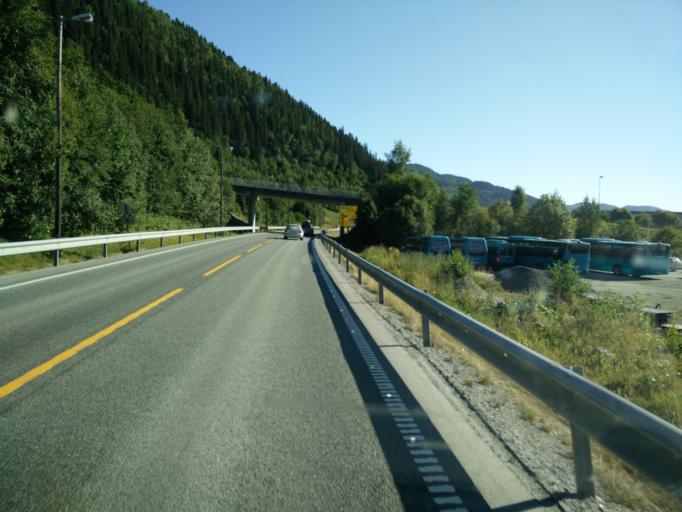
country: NO
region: Sor-Trondelag
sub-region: Orkdal
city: Orkanger
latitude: 63.2989
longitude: 9.8535
